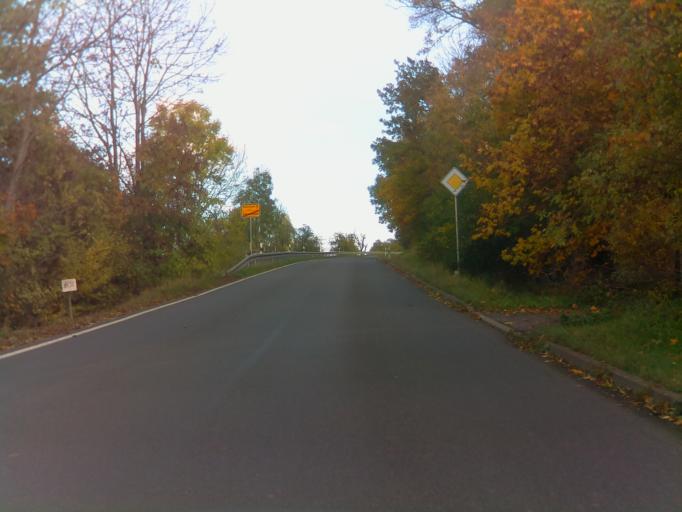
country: DE
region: Thuringia
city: Alkersleben
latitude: 50.8475
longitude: 11.0442
